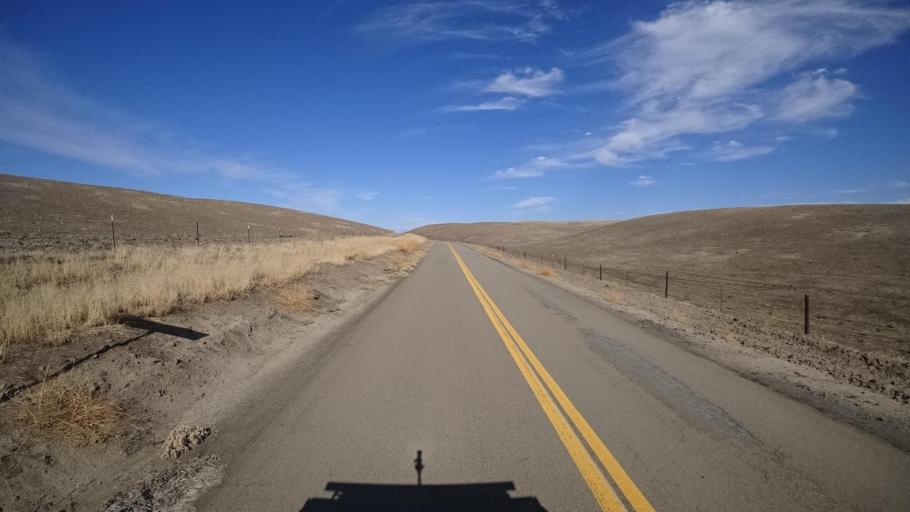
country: US
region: California
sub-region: Kern County
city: Oildale
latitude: 35.6102
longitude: -118.9448
